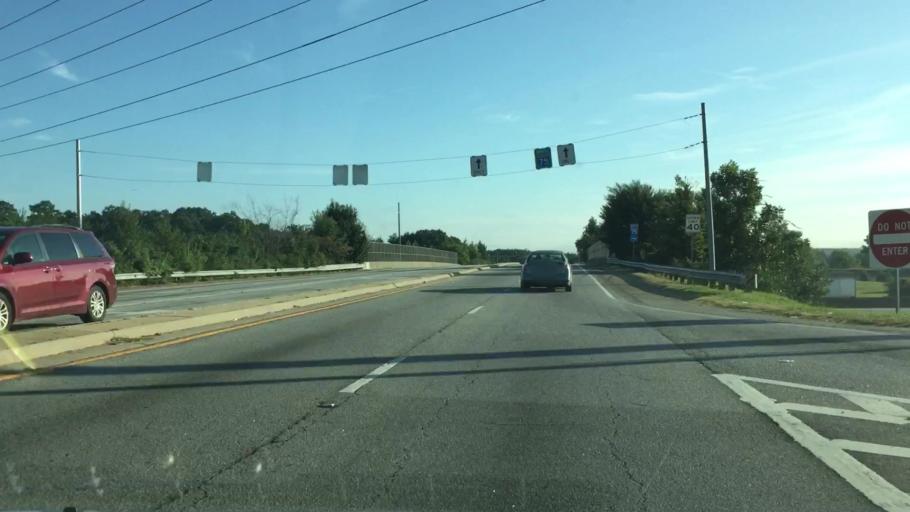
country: US
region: Georgia
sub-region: Clayton County
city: Morrow
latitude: 33.5638
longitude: -84.3210
